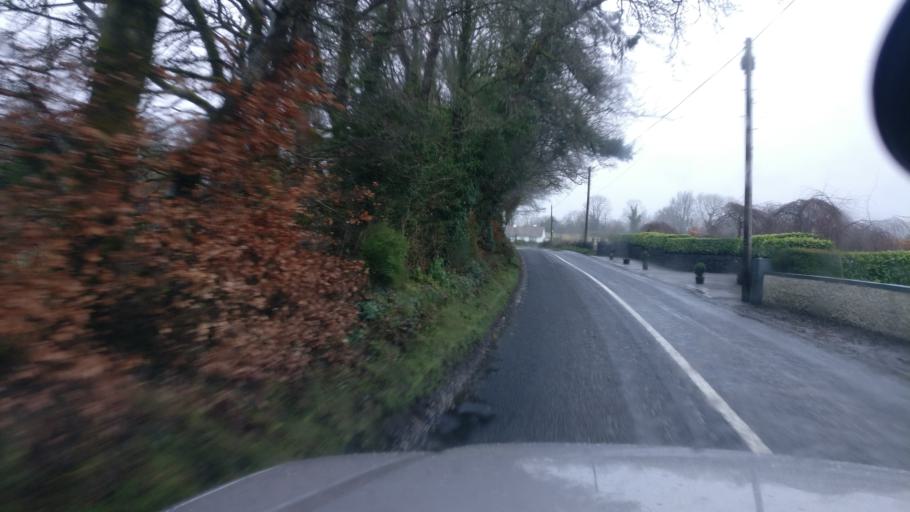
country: IE
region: Connaught
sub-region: County Galway
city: Loughrea
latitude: 53.1320
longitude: -8.4579
